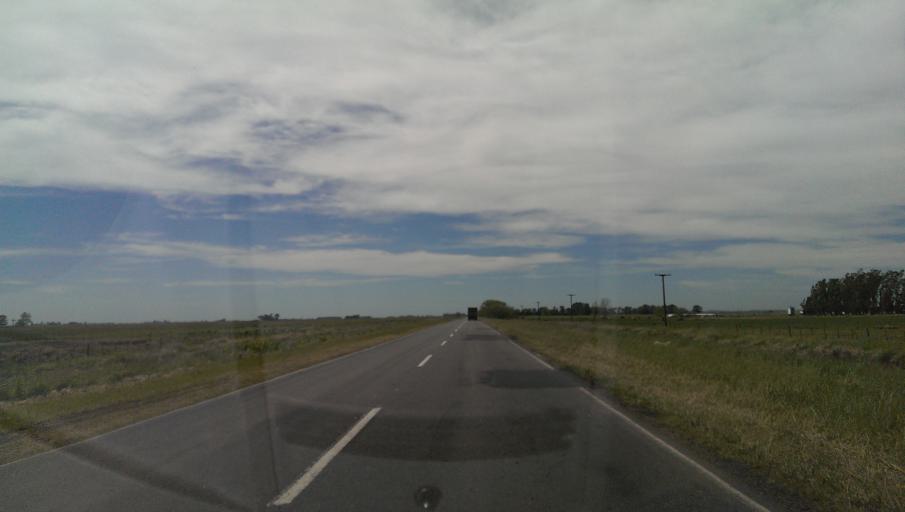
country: AR
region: Buenos Aires
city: Olavarria
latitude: -37.0309
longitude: -60.4243
